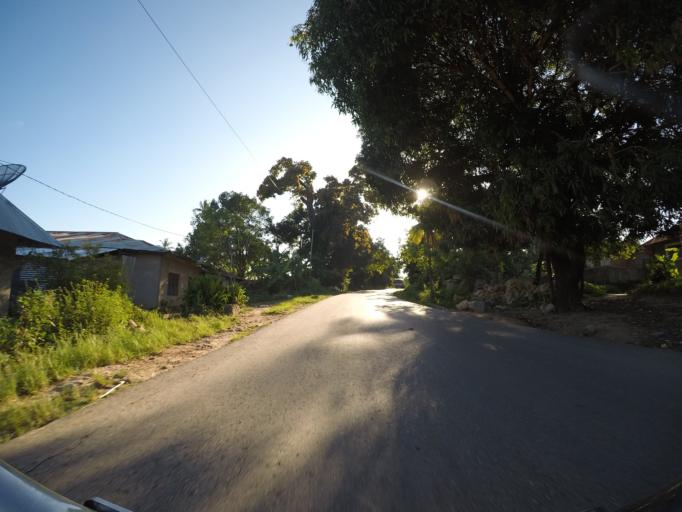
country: TZ
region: Pemba South
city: Mtambile
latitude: -5.3218
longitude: 39.7410
